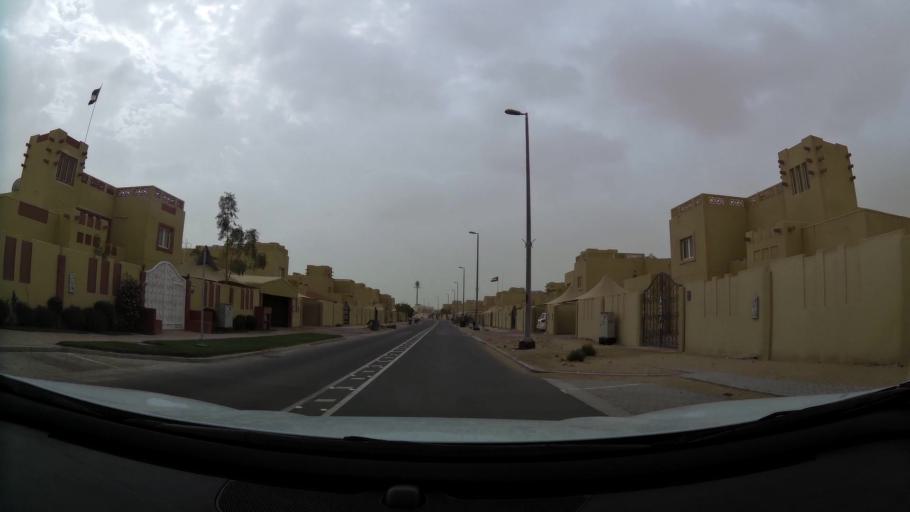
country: AE
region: Abu Dhabi
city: Abu Dhabi
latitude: 24.4601
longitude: 54.7171
